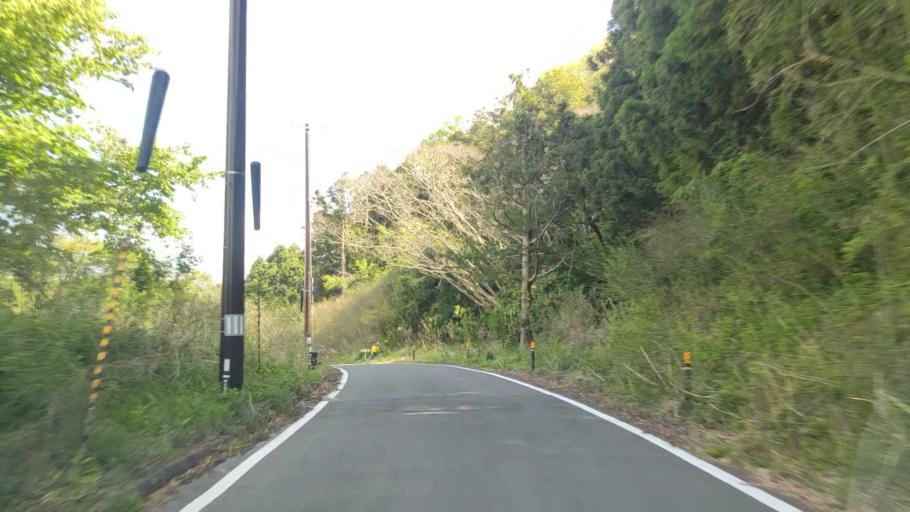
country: JP
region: Miyagi
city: Yamoto
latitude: 38.3361
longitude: 141.1605
